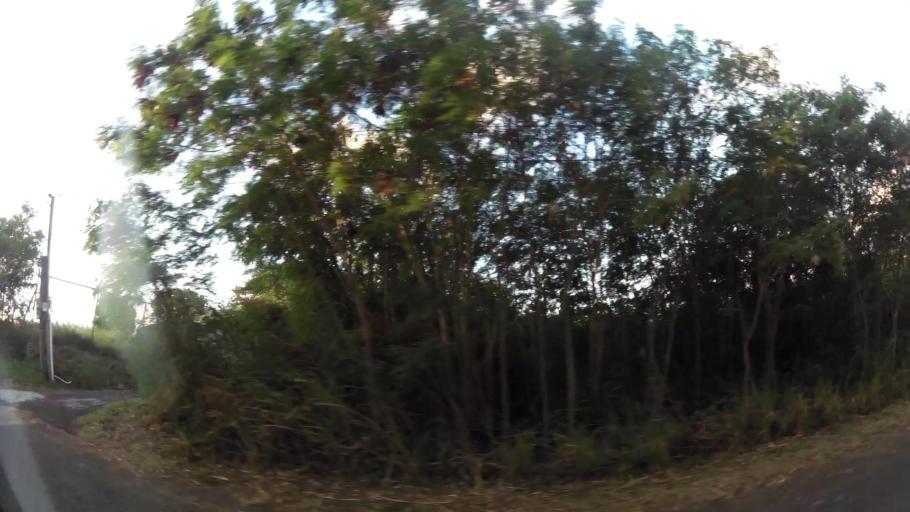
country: LC
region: Gros-Islet
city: Gros Islet
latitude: 14.0664
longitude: -60.9494
